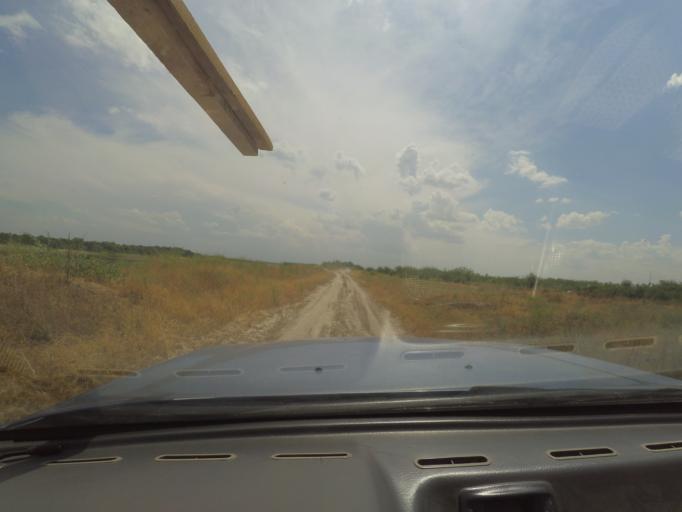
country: TJ
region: Viloyati Sughd
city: Buston
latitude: 40.5400
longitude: 69.0791
